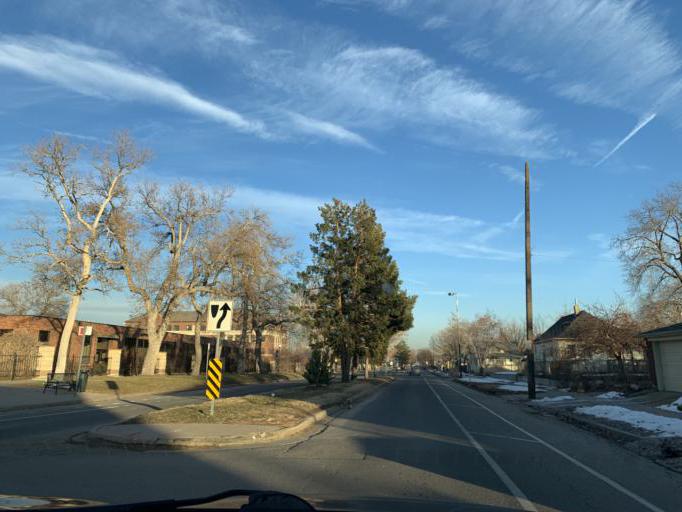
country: US
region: Colorado
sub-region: Adams County
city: Berkley
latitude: 39.7874
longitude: -105.0332
